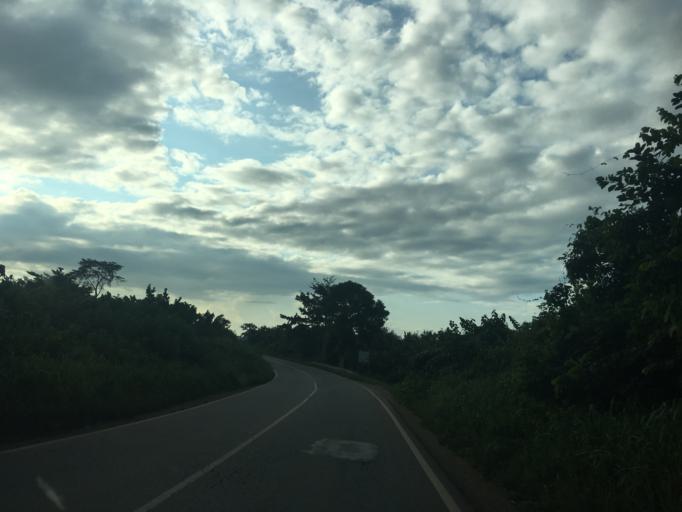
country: GH
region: Western
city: Bibiani
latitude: 6.3524
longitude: -2.2794
